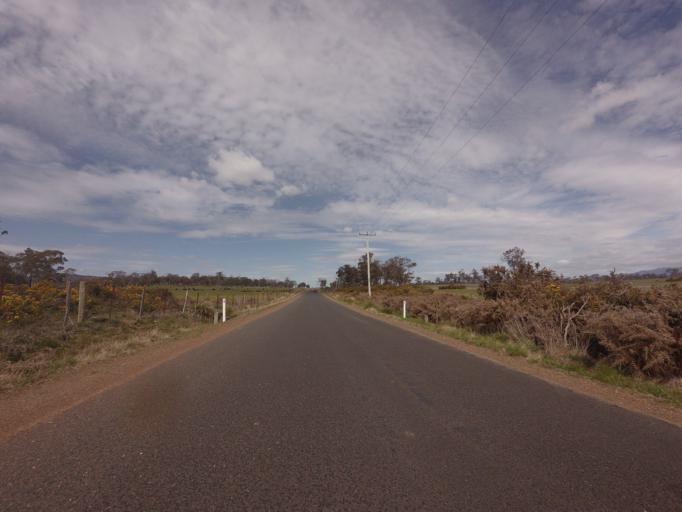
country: AU
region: Tasmania
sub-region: Northern Midlands
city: Longford
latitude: -41.7227
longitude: 147.1899
